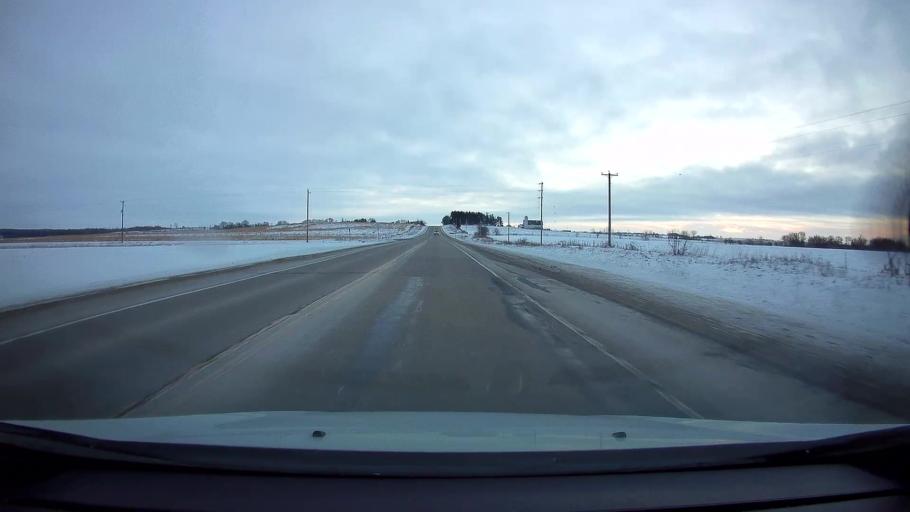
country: US
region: Wisconsin
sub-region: Saint Croix County
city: New Richmond
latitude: 45.1370
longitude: -92.5197
